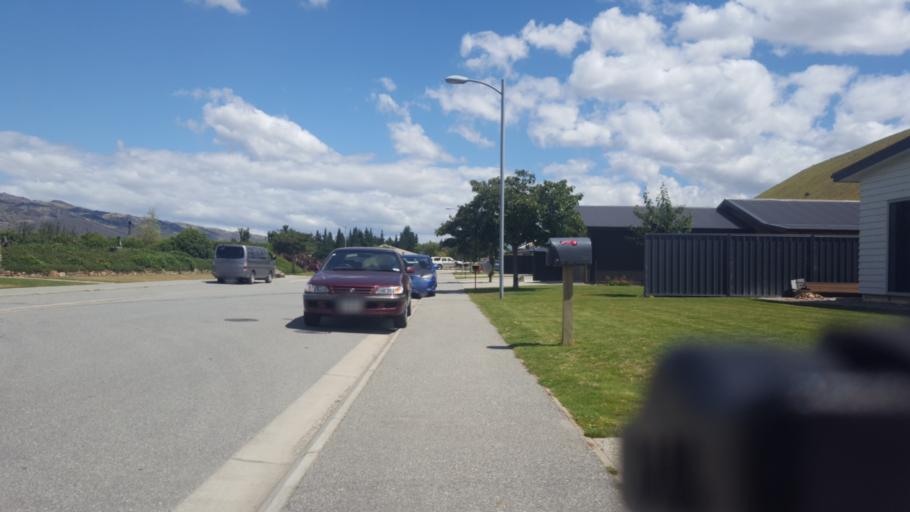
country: NZ
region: Otago
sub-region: Queenstown-Lakes District
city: Wanaka
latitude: -44.9808
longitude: 169.2351
